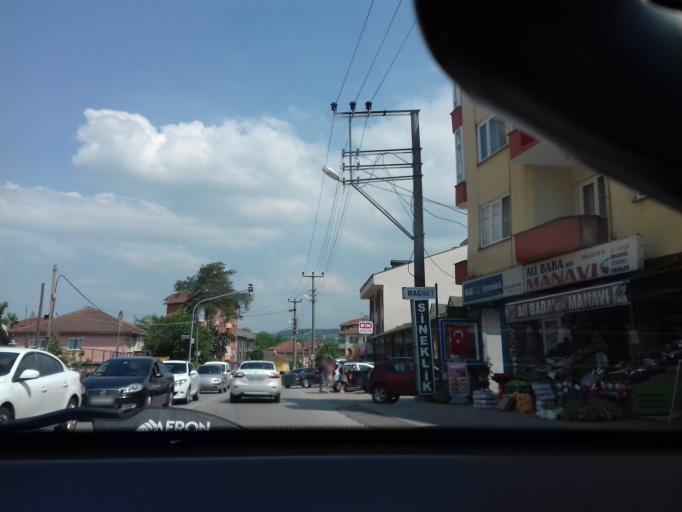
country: TR
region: Sakarya
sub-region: Merkez
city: Sapanca
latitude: 40.6896
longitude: 30.2618
